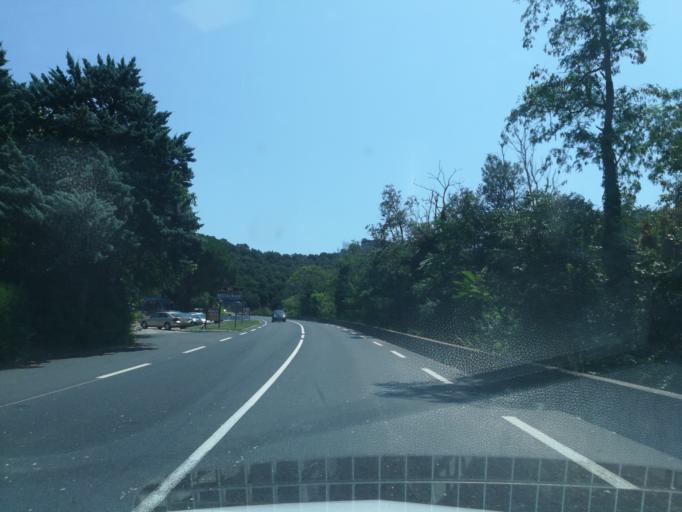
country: FR
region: Languedoc-Roussillon
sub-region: Departement des Pyrenees-Orientales
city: Maureillas-las-Illas
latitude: 42.4841
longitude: 2.8368
